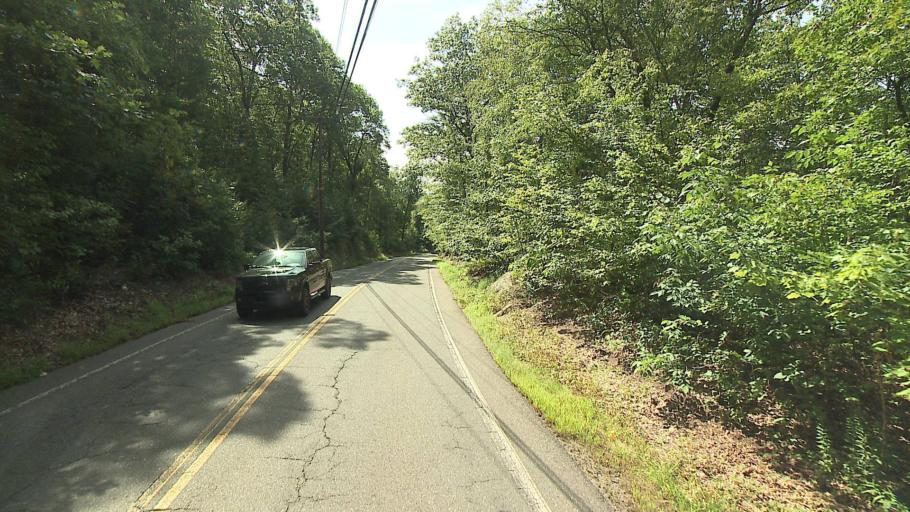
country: US
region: Connecticut
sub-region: Litchfield County
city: Oakville
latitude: 41.6241
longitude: -73.0492
